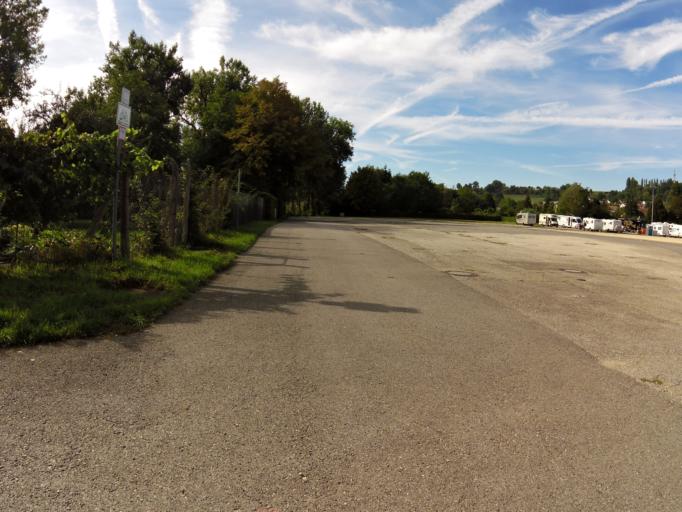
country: DE
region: Baden-Wuerttemberg
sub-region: Regierungsbezirk Stuttgart
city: Nurtingen
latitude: 48.6366
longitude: 9.3324
